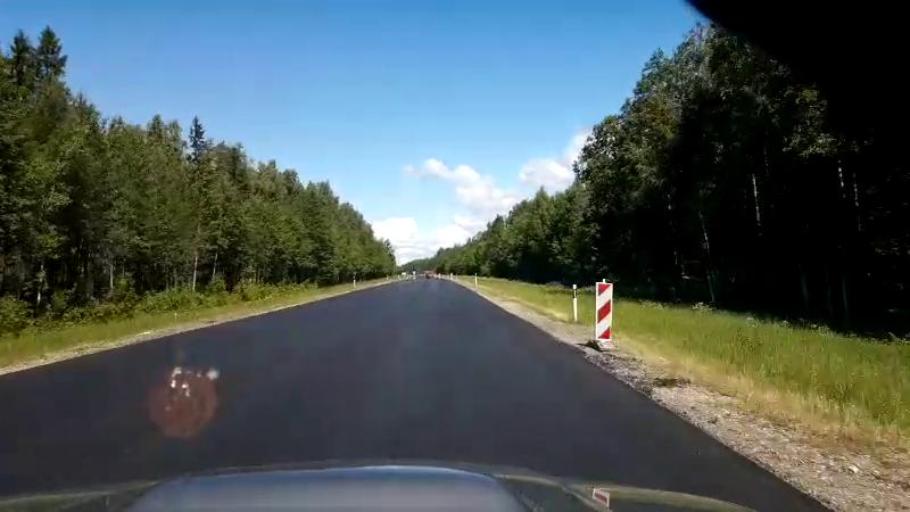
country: LV
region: Salacgrivas
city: Ainazi
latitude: 58.0275
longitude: 24.5031
